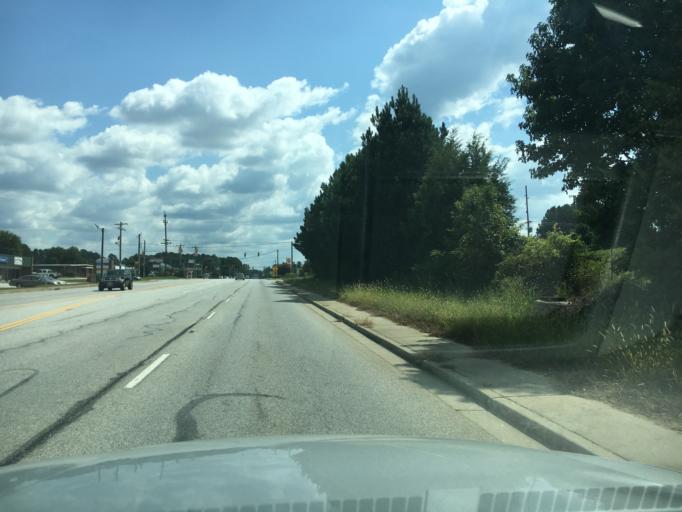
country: US
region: South Carolina
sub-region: Greenwood County
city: Greenwood
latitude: 34.2049
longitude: -82.2013
